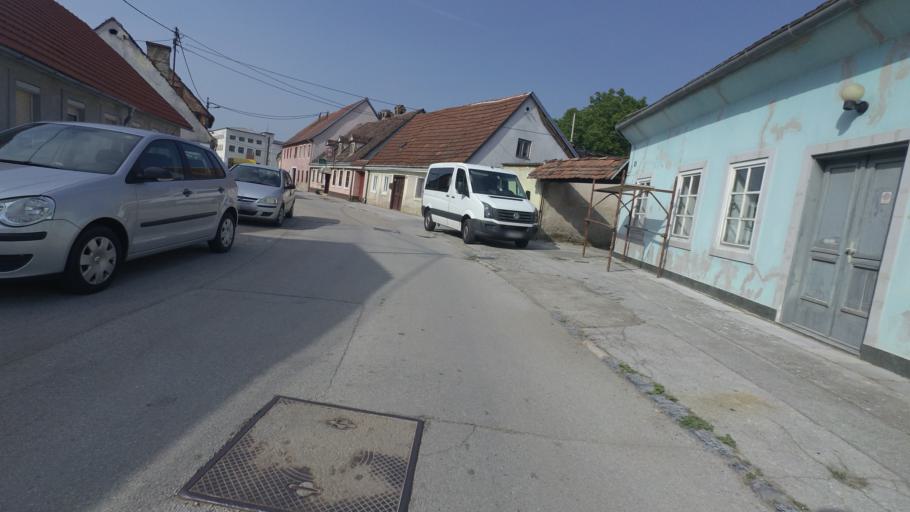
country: HR
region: Karlovacka
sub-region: Grad Karlovac
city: Karlovac
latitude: 45.4983
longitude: 15.5551
